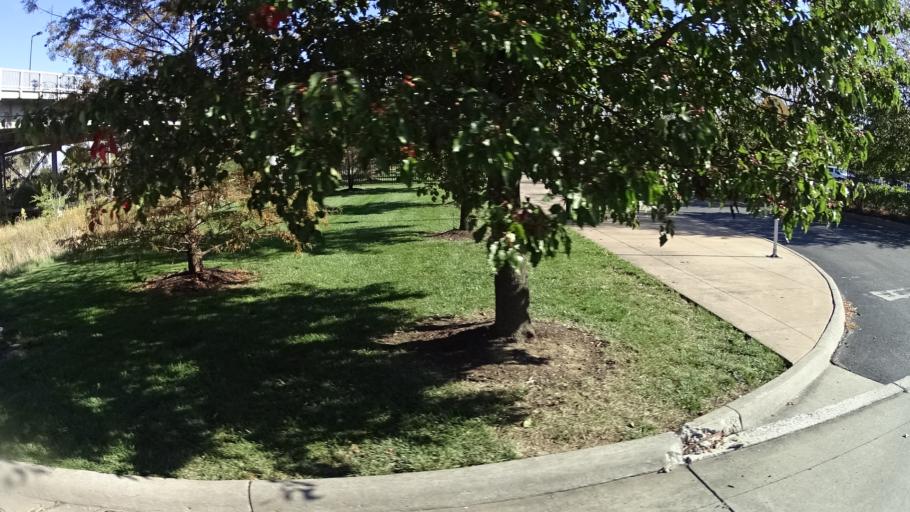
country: US
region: Ohio
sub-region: Lorain County
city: Lorain
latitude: 41.4685
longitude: -82.1771
